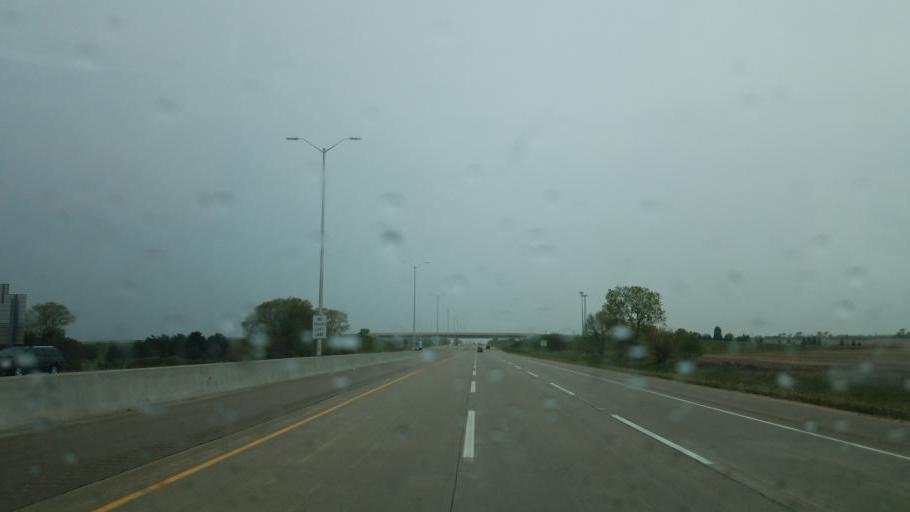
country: US
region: Illinois
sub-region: Kane County
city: Hampshire
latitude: 42.1497
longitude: -88.5313
